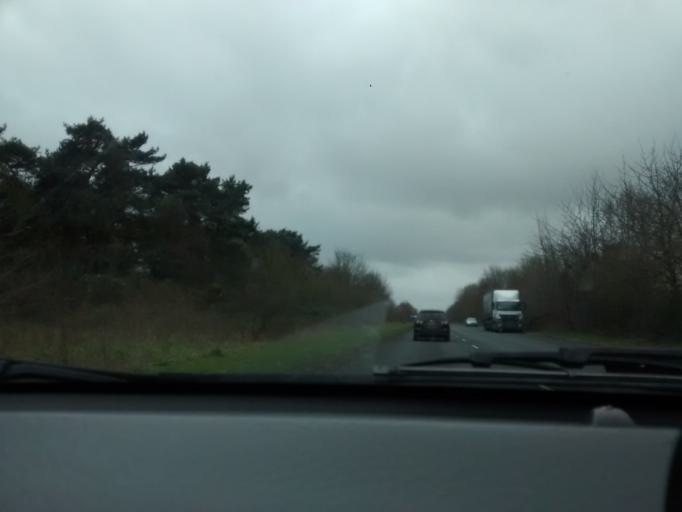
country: GB
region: England
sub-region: Suffolk
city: Felixstowe
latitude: 51.9730
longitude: 1.3452
